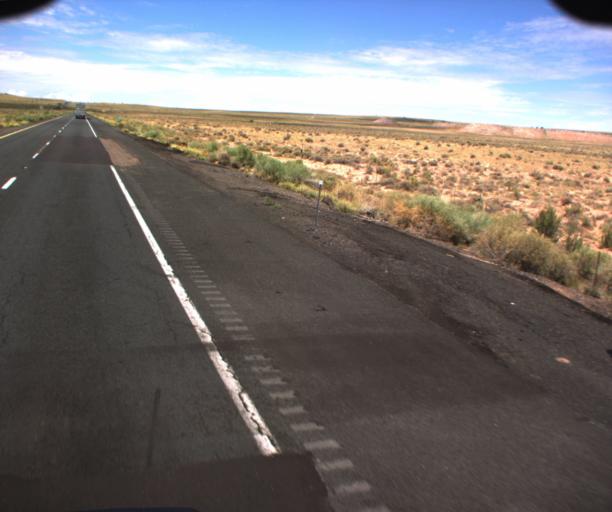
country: US
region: Arizona
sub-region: Apache County
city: Houck
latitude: 35.1118
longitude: -109.5893
